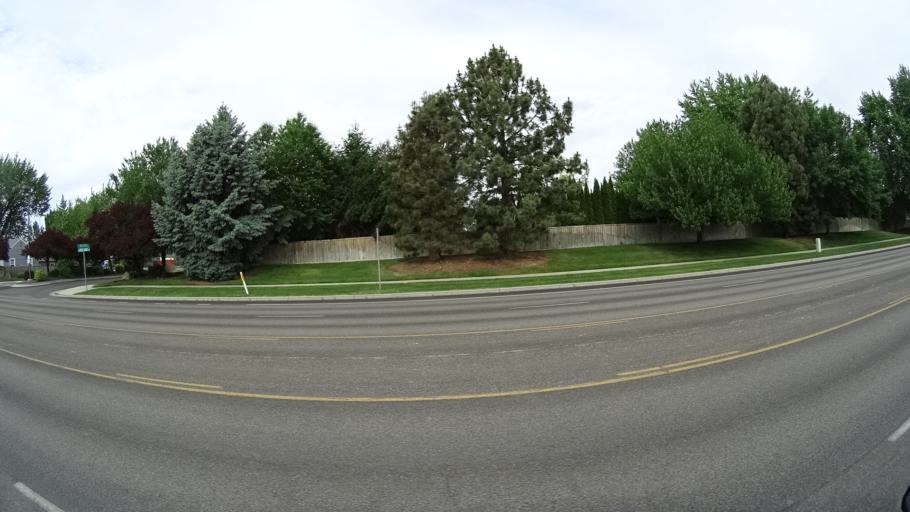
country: US
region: Idaho
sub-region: Ada County
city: Meridian
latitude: 43.6152
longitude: -116.3744
